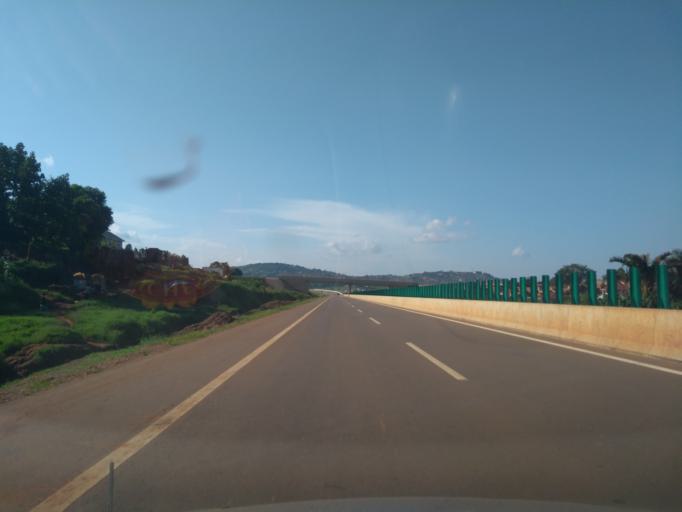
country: UG
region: Central Region
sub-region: Wakiso District
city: Kajansi
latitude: 0.2068
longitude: 32.5287
